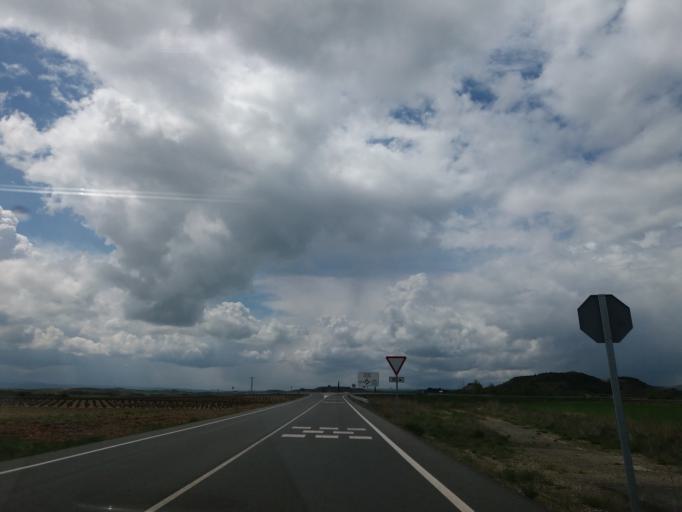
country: ES
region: La Rioja
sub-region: Provincia de La Rioja
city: Sajazarra
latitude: 42.5709
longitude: -2.9556
